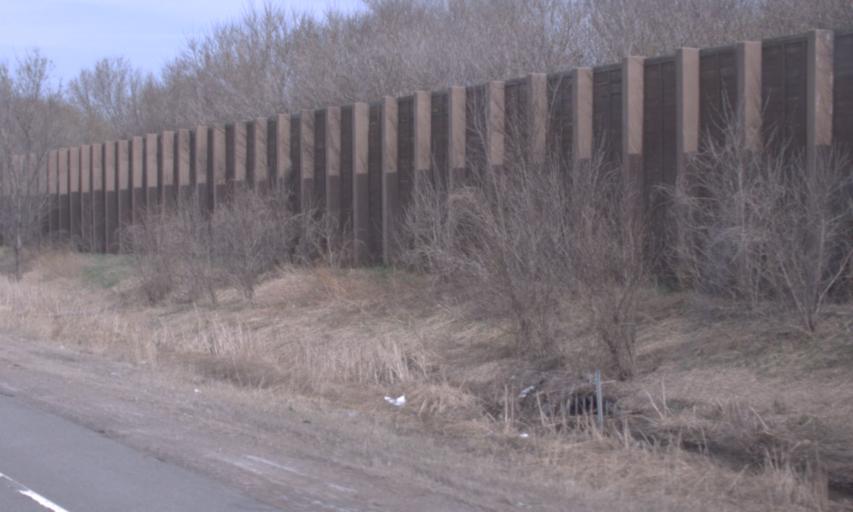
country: US
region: Minnesota
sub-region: Anoka County
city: Coon Rapids
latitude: 45.1581
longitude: -93.2801
